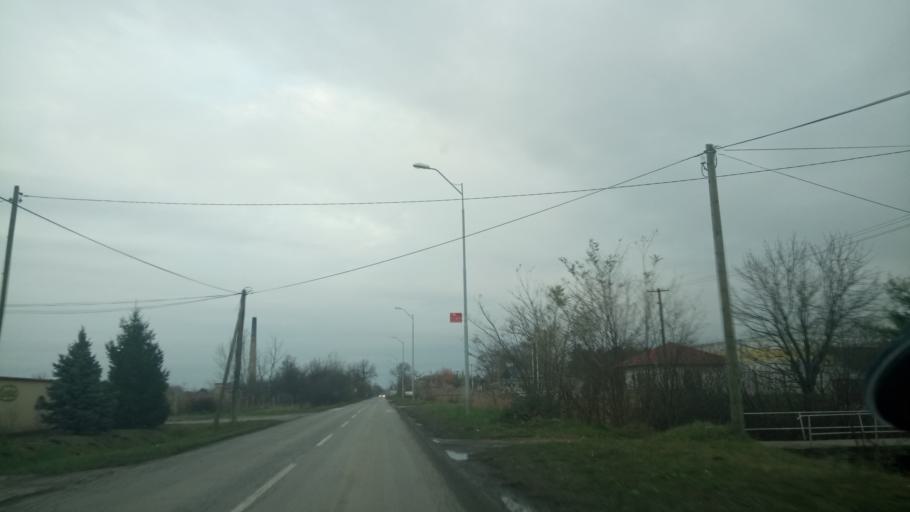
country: RS
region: Autonomna Pokrajina Vojvodina
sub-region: Sremski Okrug
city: Stara Pazova
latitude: 44.9703
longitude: 20.1629
